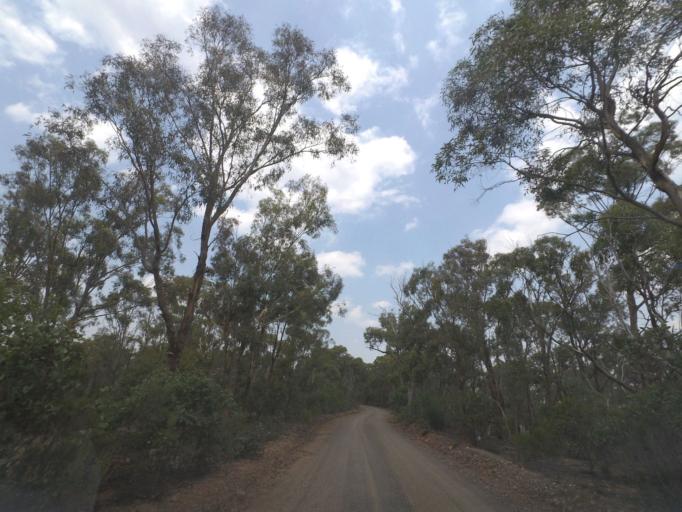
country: AU
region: Victoria
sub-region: Moorabool
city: Bacchus Marsh
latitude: -37.5942
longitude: 144.4422
